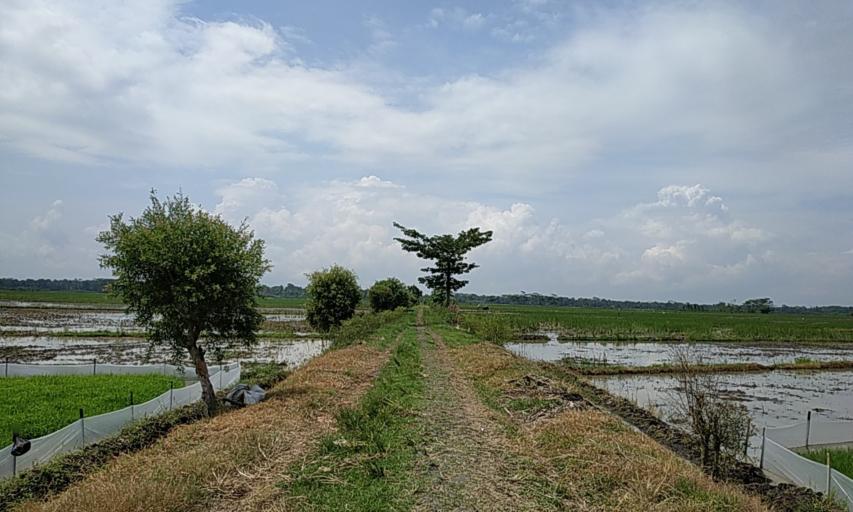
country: ID
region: Central Java
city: Kedungbulu
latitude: -7.5304
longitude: 108.7864
